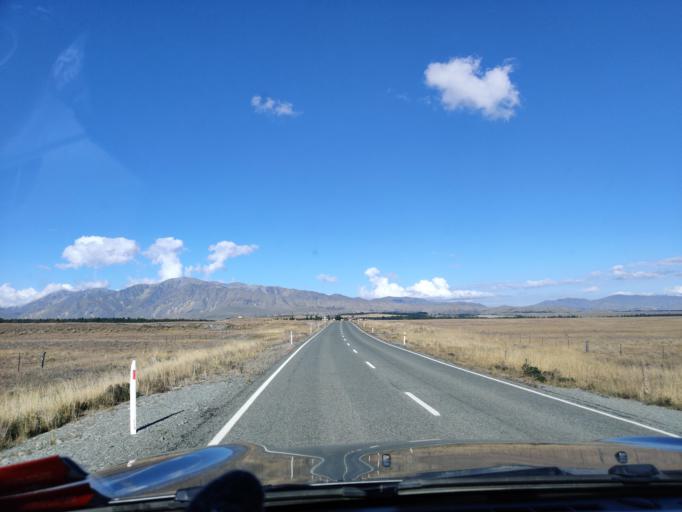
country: NZ
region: Canterbury
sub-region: Timaru District
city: Pleasant Point
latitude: -43.9985
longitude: 170.4296
